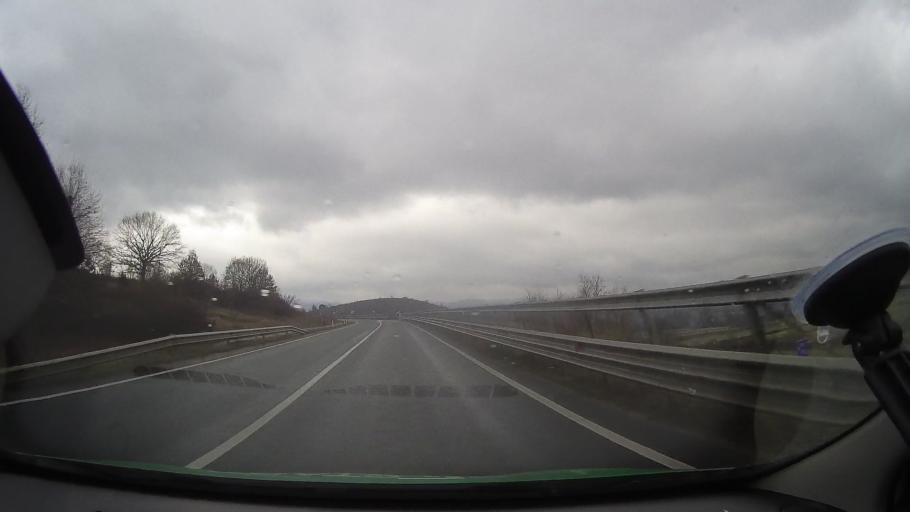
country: RO
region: Hunedoara
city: Vata de Jos
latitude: 46.2102
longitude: 22.5801
